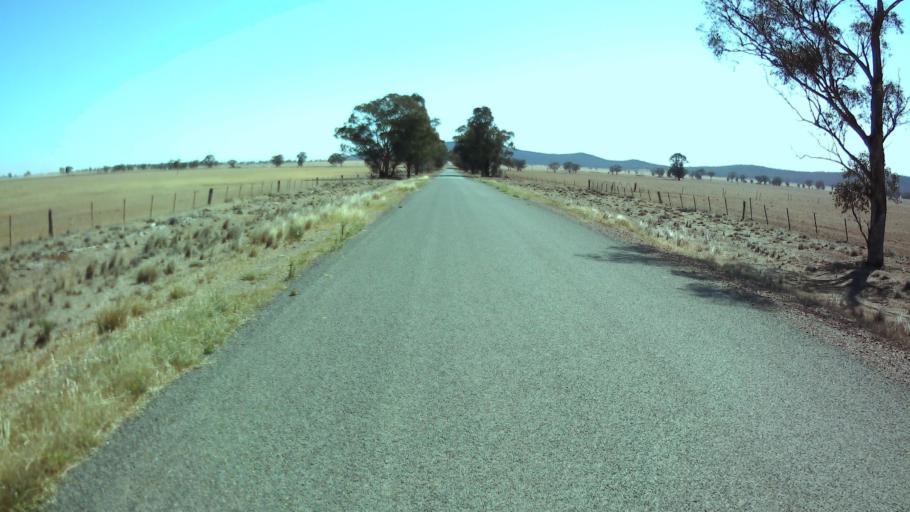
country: AU
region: New South Wales
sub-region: Weddin
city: Grenfell
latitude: -33.7105
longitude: 147.9119
